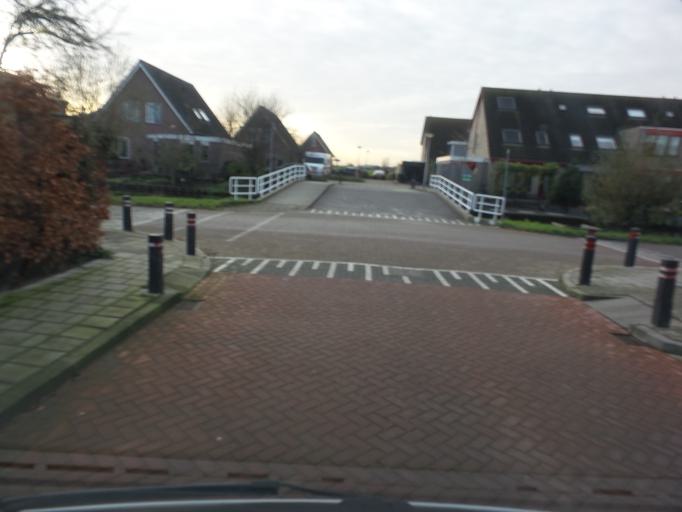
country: NL
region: Utrecht
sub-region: Gemeente Oudewater
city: Oudewater
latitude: 52.0590
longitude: 4.8224
